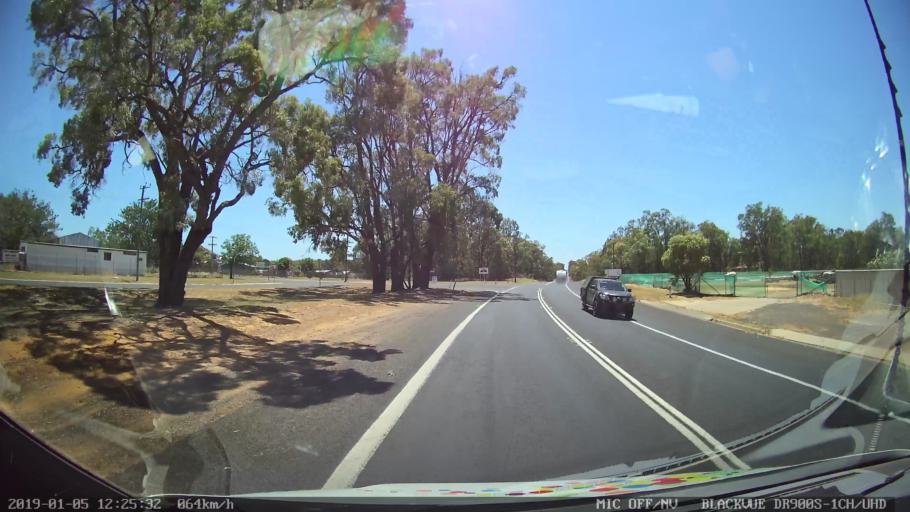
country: AU
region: New South Wales
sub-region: Warrumbungle Shire
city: Coonabarabran
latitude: -31.2597
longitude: 149.2855
